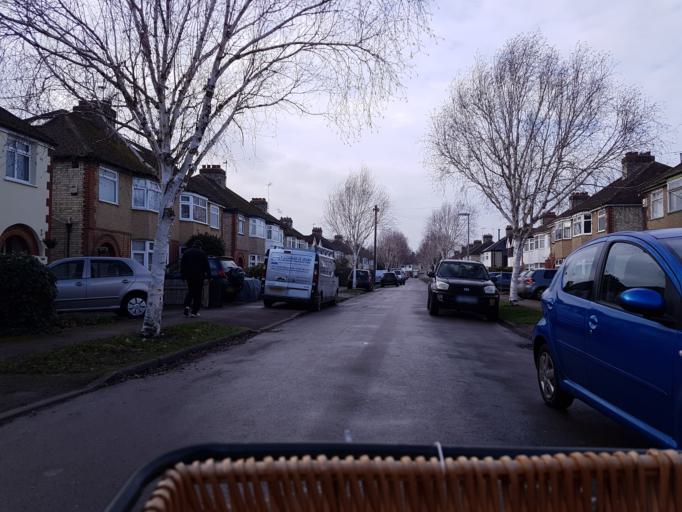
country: GB
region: England
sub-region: Cambridgeshire
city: Cambridge
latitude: 52.1910
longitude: 0.1529
